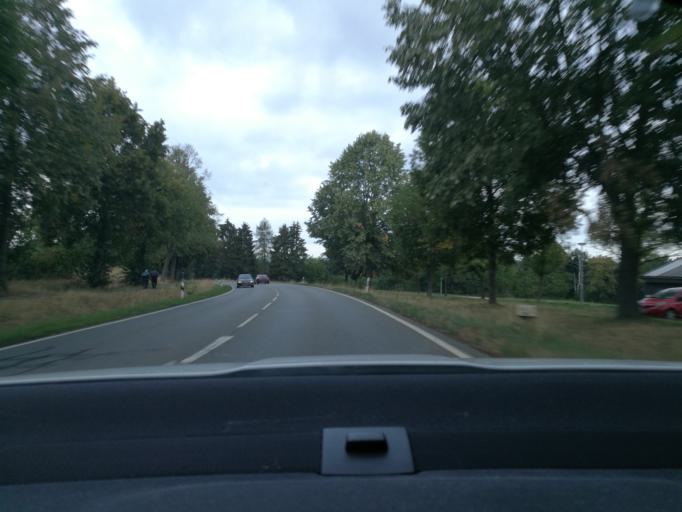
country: DE
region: Hesse
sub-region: Regierungsbezirk Giessen
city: Limburg an der Lahn
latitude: 50.3747
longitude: 8.0801
